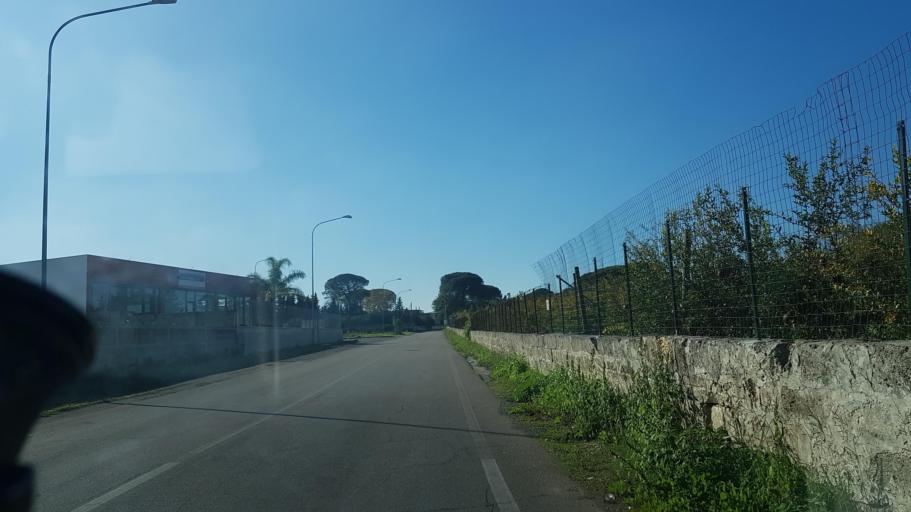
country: IT
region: Apulia
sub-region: Provincia di Lecce
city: Arnesano
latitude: 40.3352
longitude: 18.1043
